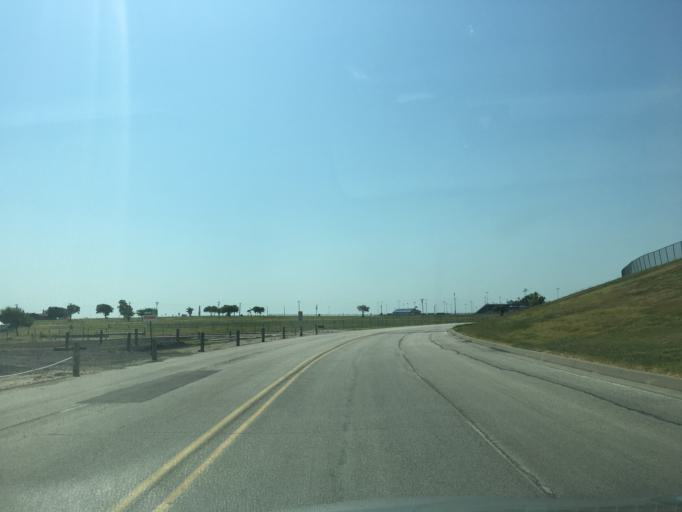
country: US
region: Texas
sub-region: Denton County
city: Justin
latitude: 33.0404
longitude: -97.2778
